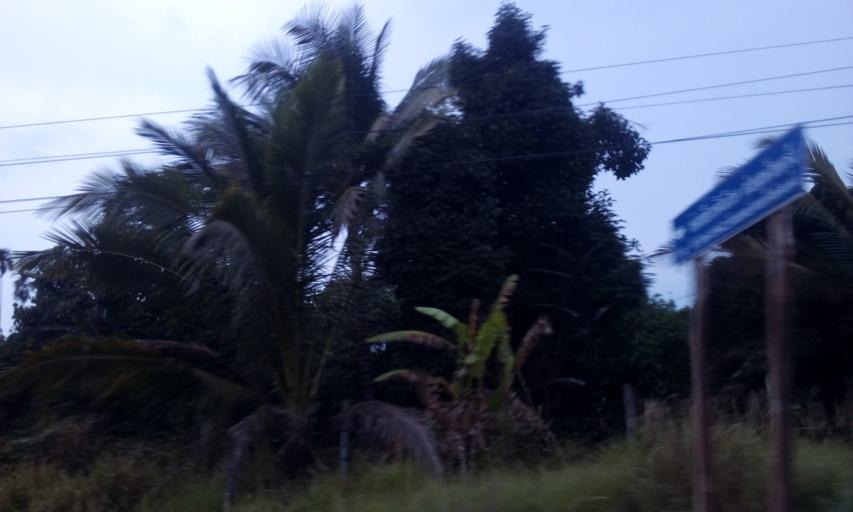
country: TH
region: Trat
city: Khao Saming
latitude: 12.3626
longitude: 102.3844
